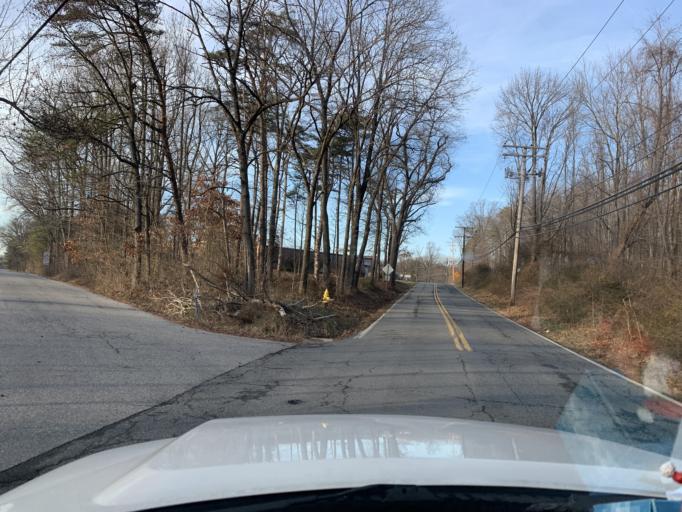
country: US
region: Maryland
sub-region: Anne Arundel County
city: Jessup
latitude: 39.1445
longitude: -76.7578
